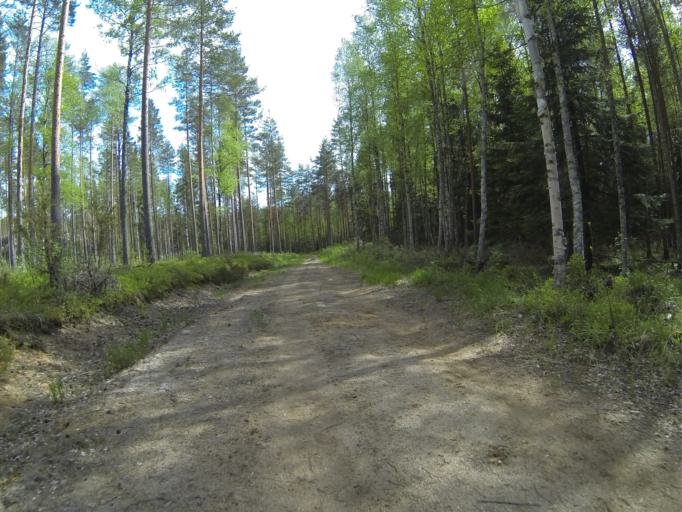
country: FI
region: Varsinais-Suomi
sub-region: Salo
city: Salo
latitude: 60.3871
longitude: 23.2043
